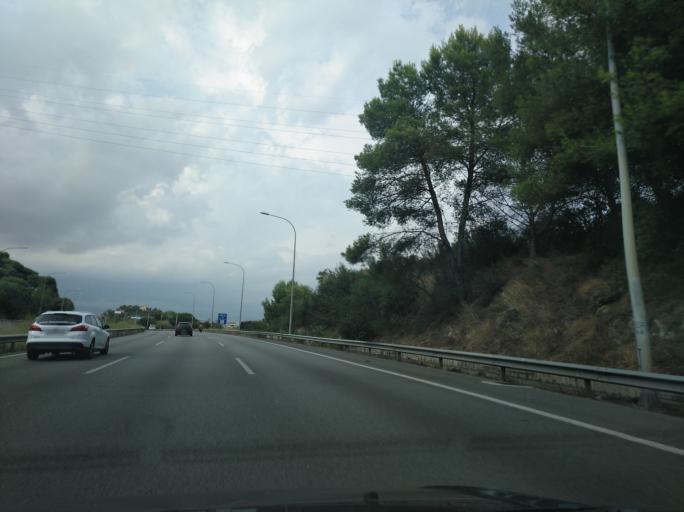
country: ES
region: Catalonia
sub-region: Provincia de Barcelona
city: Montcada i Reixac
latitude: 41.4782
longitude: 2.1845
